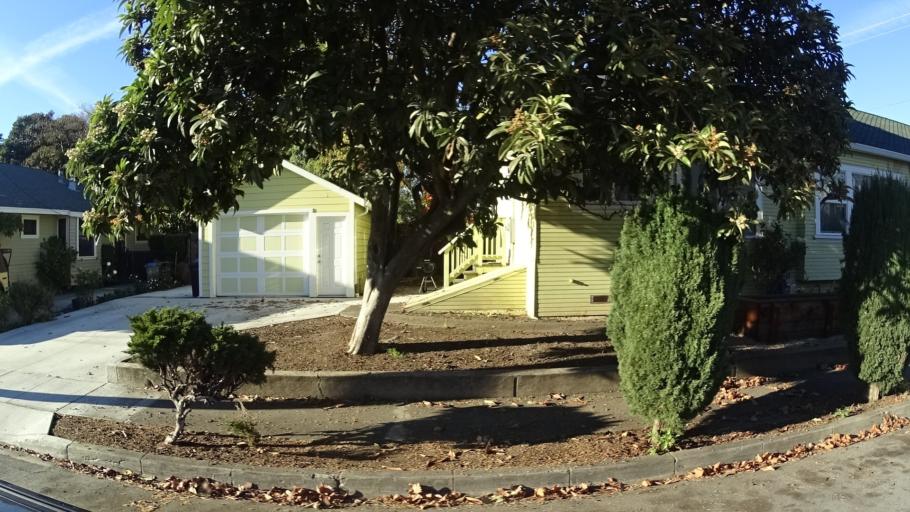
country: US
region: California
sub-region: Santa Clara County
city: San Jose
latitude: 37.3460
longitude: -121.9015
